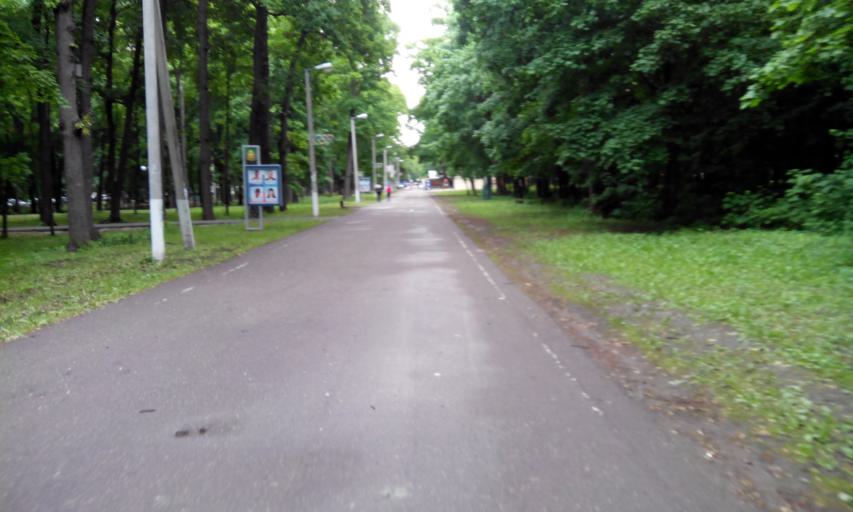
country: RU
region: Penza
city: Penza
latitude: 53.1827
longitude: 44.9875
